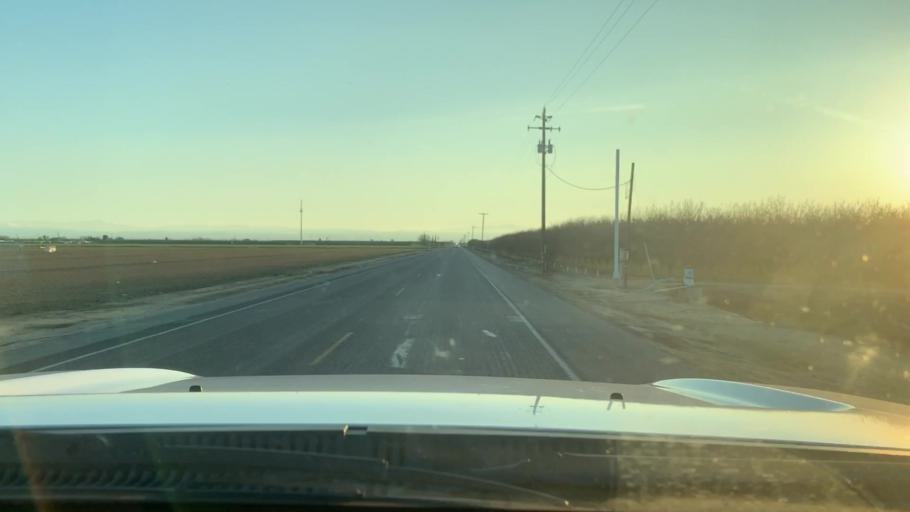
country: US
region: California
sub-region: Kern County
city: Wasco
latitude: 35.5001
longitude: -119.3767
